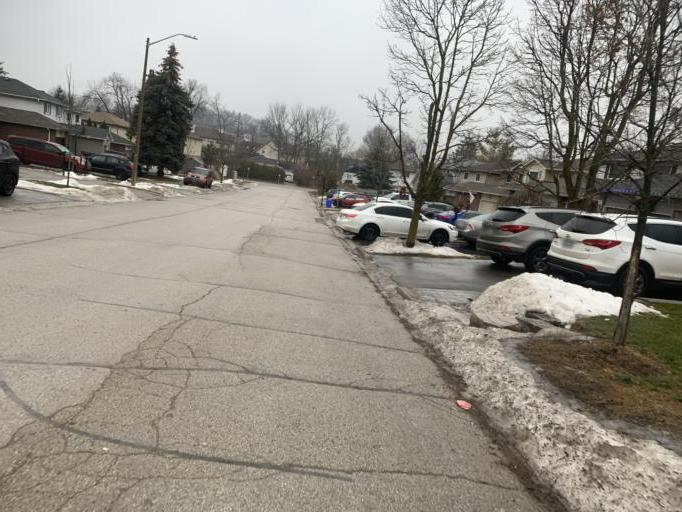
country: CA
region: Ontario
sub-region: Halton
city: Milton
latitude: 43.6590
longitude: -79.9167
